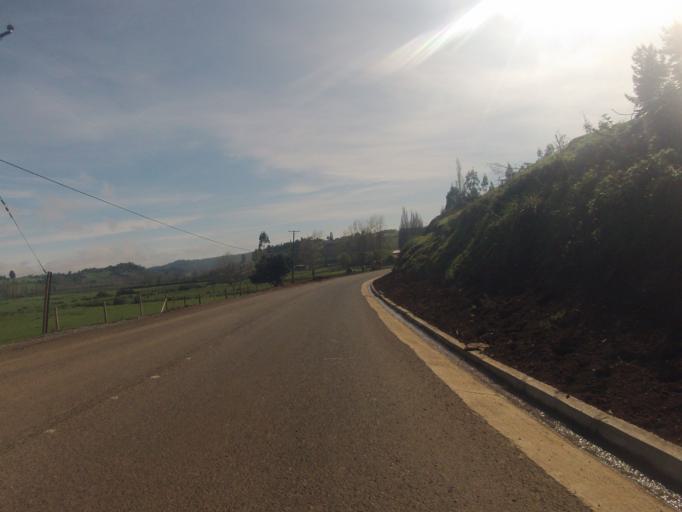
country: CL
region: Araucania
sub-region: Provincia de Cautin
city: Temuco
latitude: -38.7126
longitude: -72.5994
